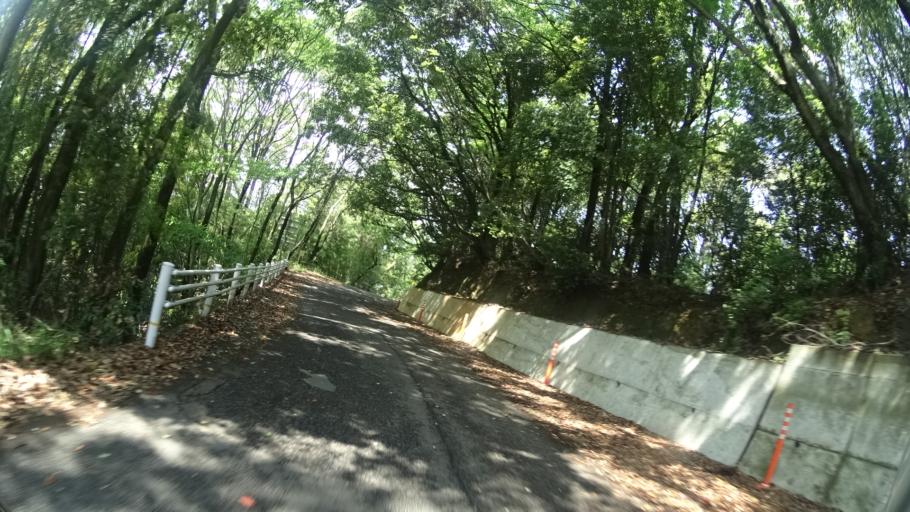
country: JP
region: Tokushima
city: Tokushima-shi
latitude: 34.0679
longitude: 134.5142
